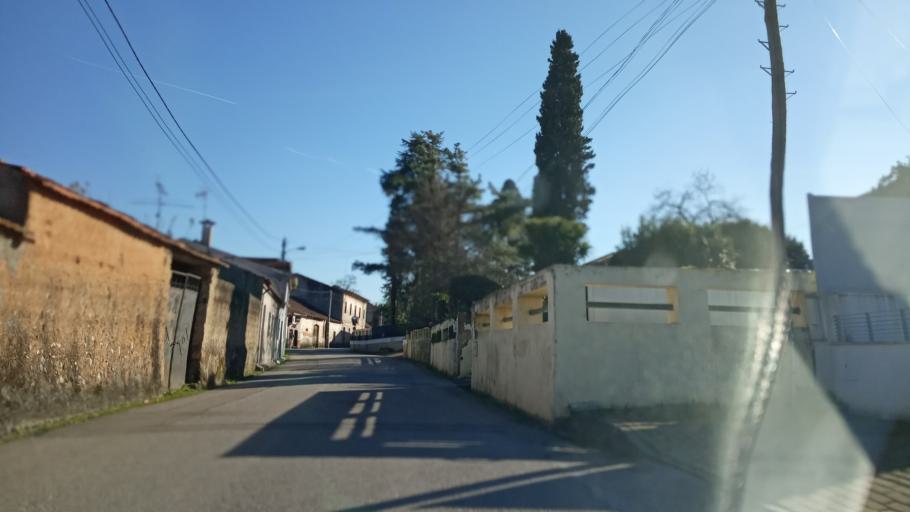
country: PT
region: Aveiro
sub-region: Anadia
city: Anadia
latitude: 40.4286
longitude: -8.4286
